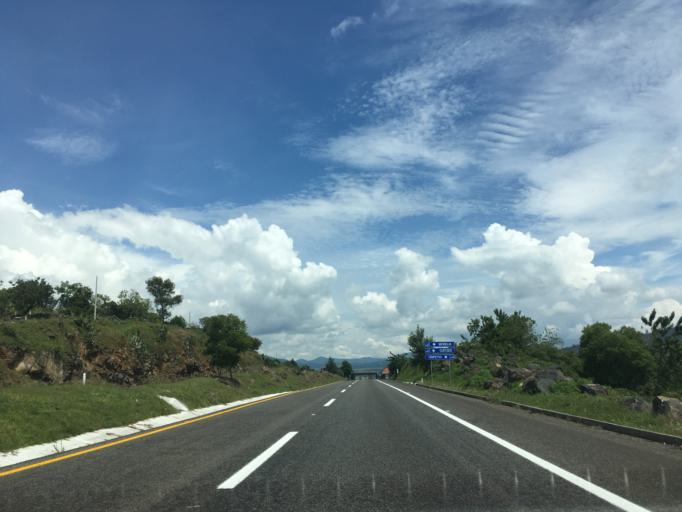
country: MX
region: Michoacan
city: Acuitzio del Canje
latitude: 19.5542
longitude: -101.3483
